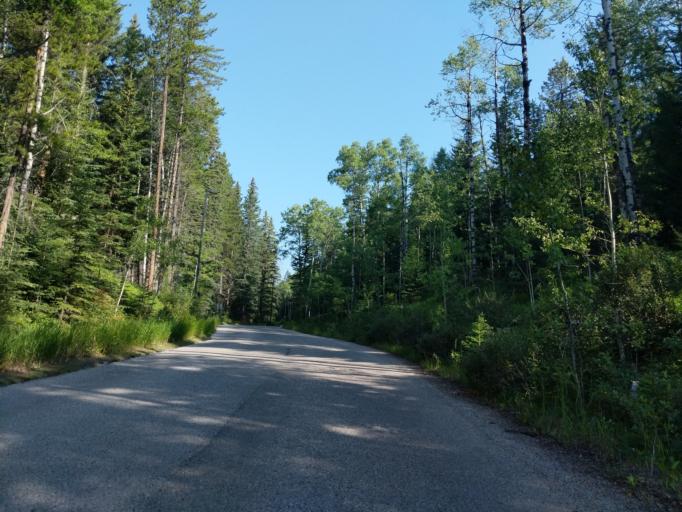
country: CA
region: Alberta
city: Canmore
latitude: 51.1011
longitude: -115.3432
